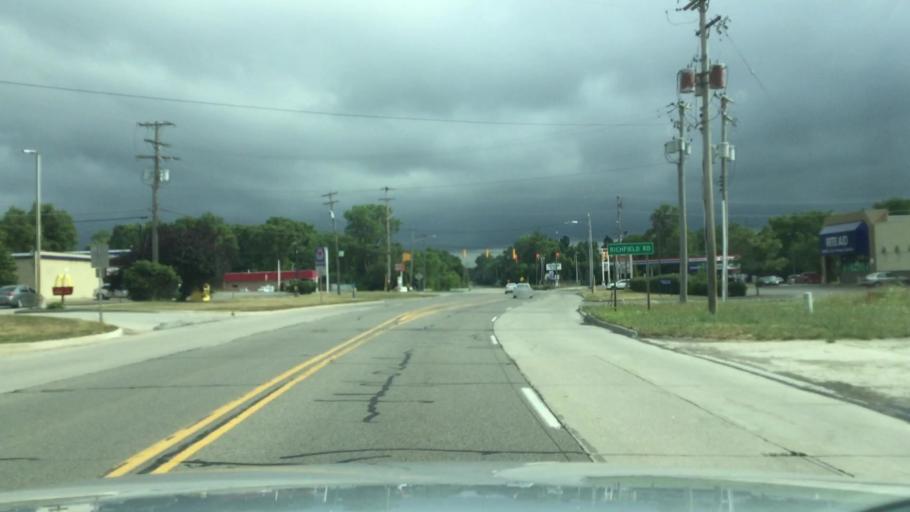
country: US
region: Michigan
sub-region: Genesee County
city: Burton
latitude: 43.0526
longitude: -83.6159
